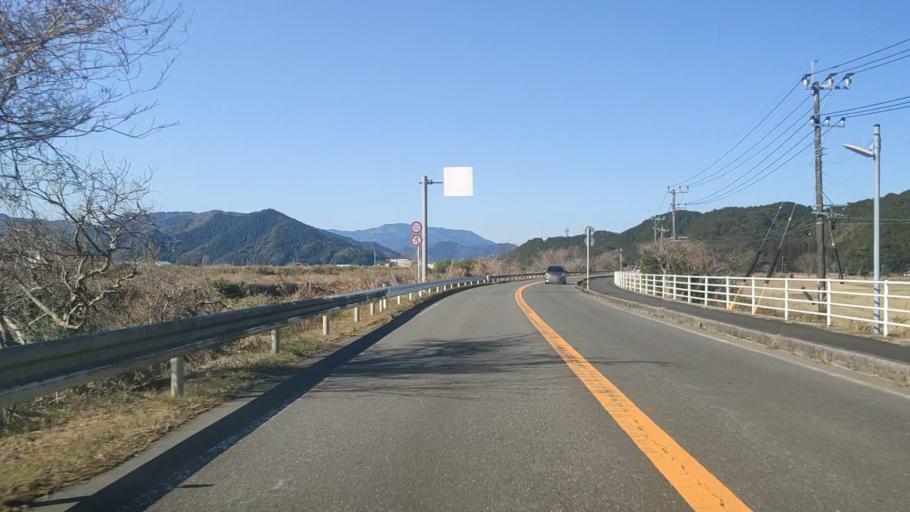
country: JP
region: Oita
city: Saiki
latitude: 32.9363
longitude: 131.9181
